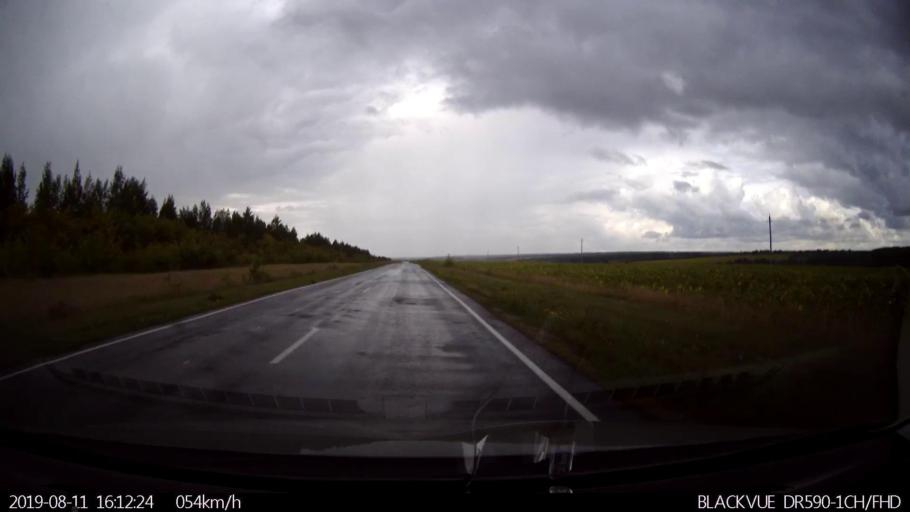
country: RU
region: Ulyanovsk
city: Ignatovka
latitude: 54.0112
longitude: 47.6405
